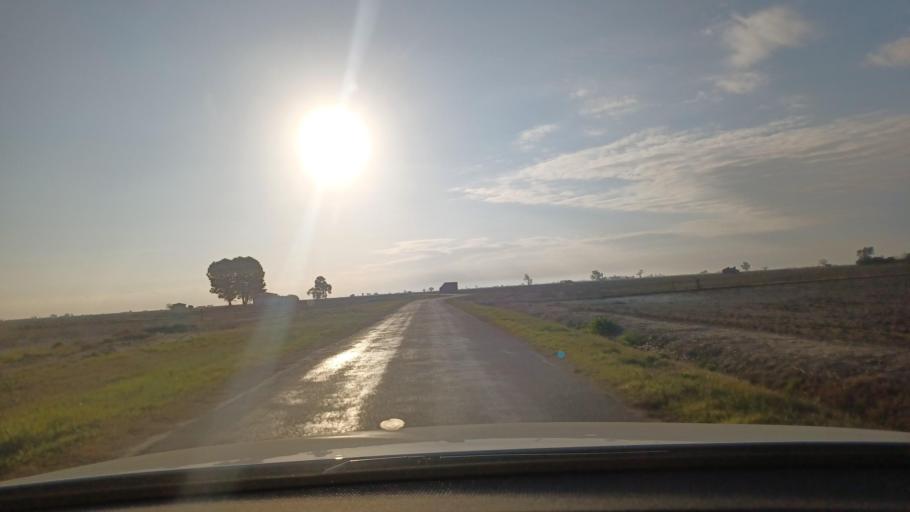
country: ES
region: Catalonia
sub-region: Provincia de Tarragona
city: Deltebre
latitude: 40.6981
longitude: 0.6466
